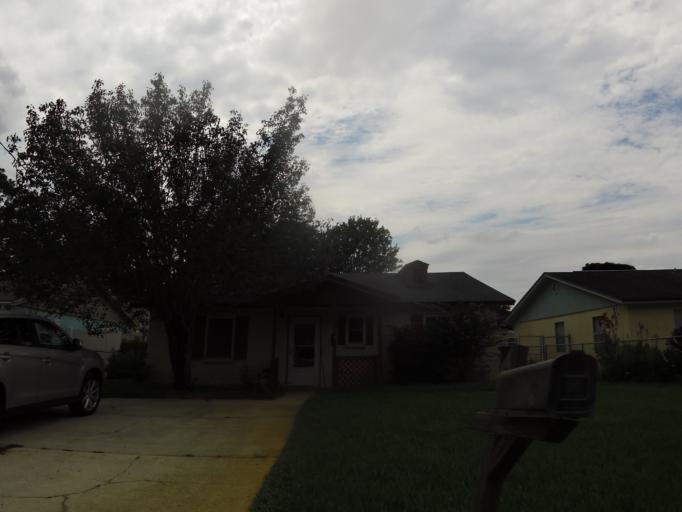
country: US
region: Florida
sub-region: Duval County
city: Atlantic Beach
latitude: 30.3317
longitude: -81.4201
